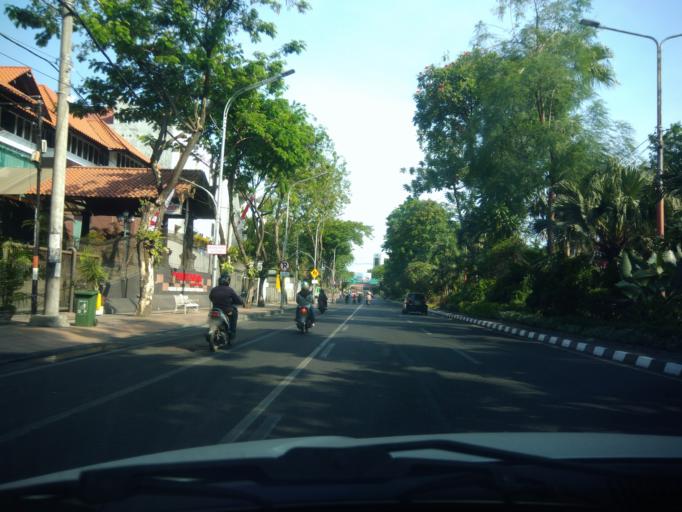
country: ID
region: East Java
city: Jagirsidosermo
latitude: -7.2935
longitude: 112.7391
